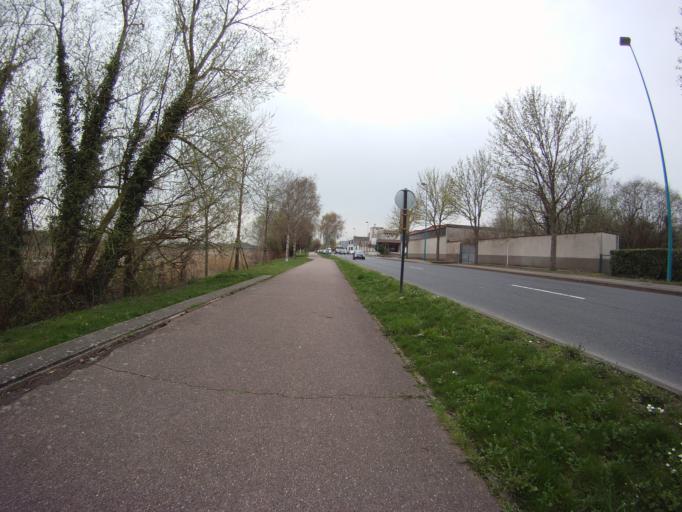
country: FR
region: Lorraine
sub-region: Departement de Meurthe-et-Moselle
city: Tomblaine
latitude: 48.6846
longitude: 6.2060
